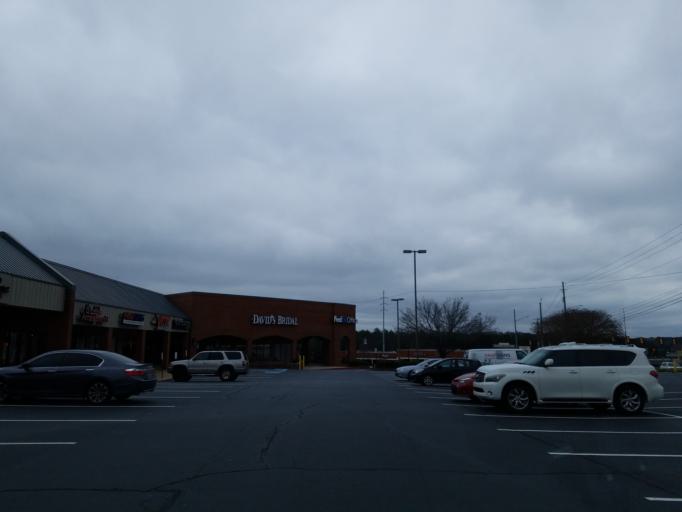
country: US
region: Georgia
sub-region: Cobb County
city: Kennesaw
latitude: 34.0137
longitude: -84.5628
